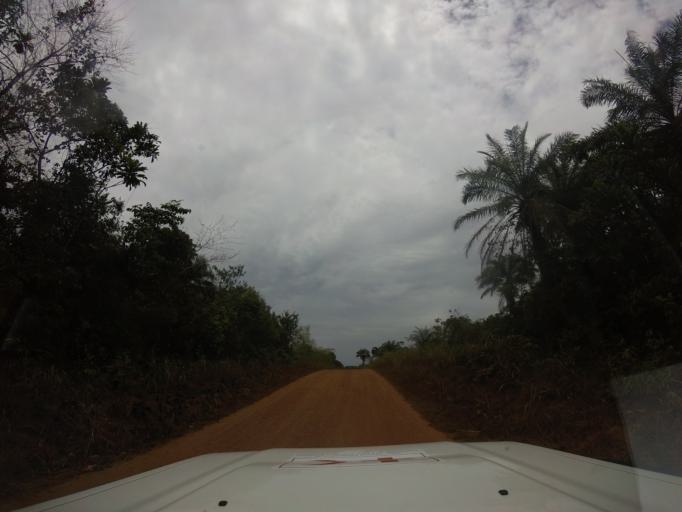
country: LR
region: Grand Cape Mount
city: Robertsport
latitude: 6.9391
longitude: -11.3292
